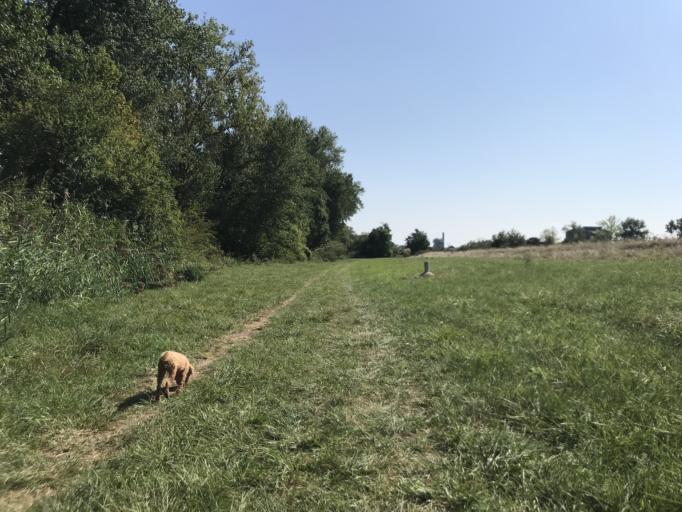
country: DE
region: Hesse
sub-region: Regierungsbezirk Darmstadt
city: Bischofsheim
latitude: 49.9990
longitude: 8.3827
